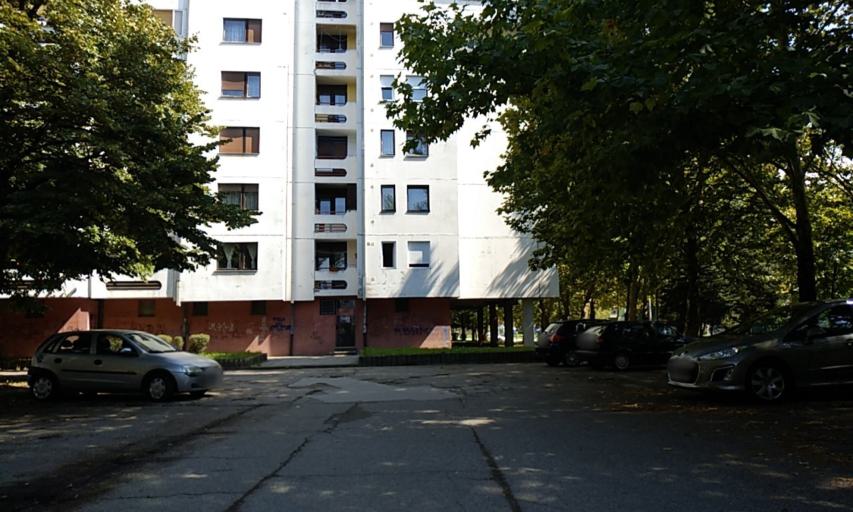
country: BA
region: Republika Srpska
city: Mejdan - Obilicevo
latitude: 44.7591
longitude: 17.1950
